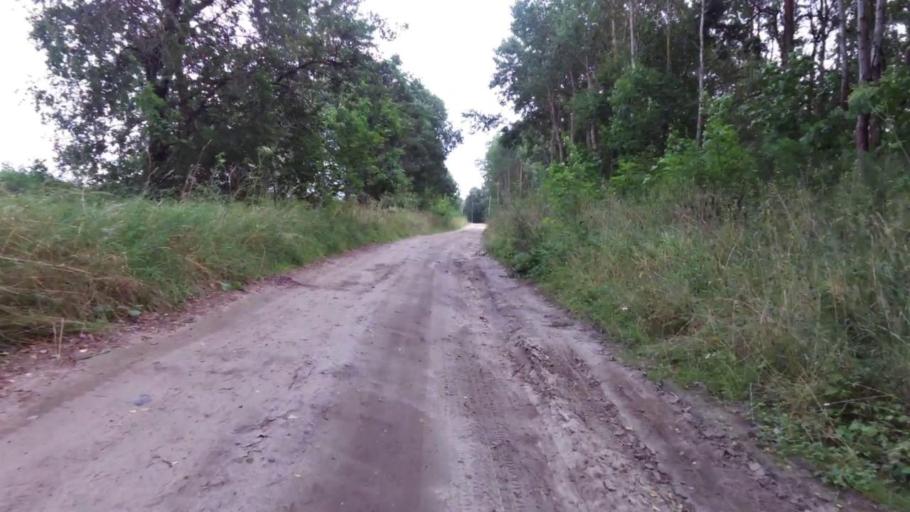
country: PL
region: West Pomeranian Voivodeship
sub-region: Powiat drawski
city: Drawsko Pomorskie
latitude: 53.5655
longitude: 15.8559
